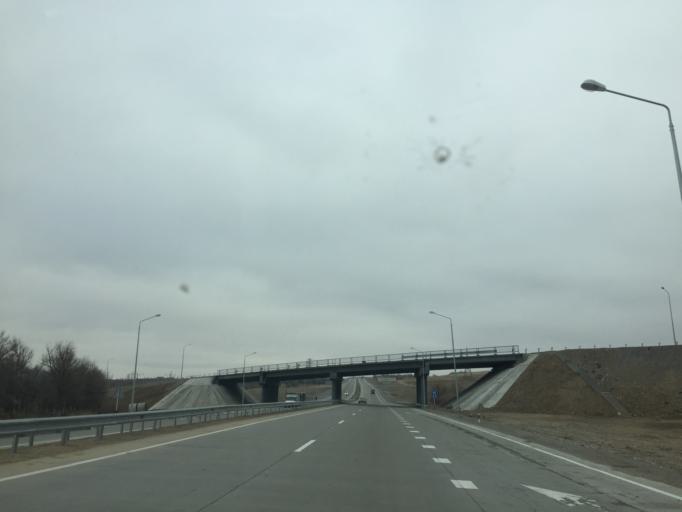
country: KZ
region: Ongtustik Qazaqstan
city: Sastobe
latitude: 42.5299
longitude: 70.0197
